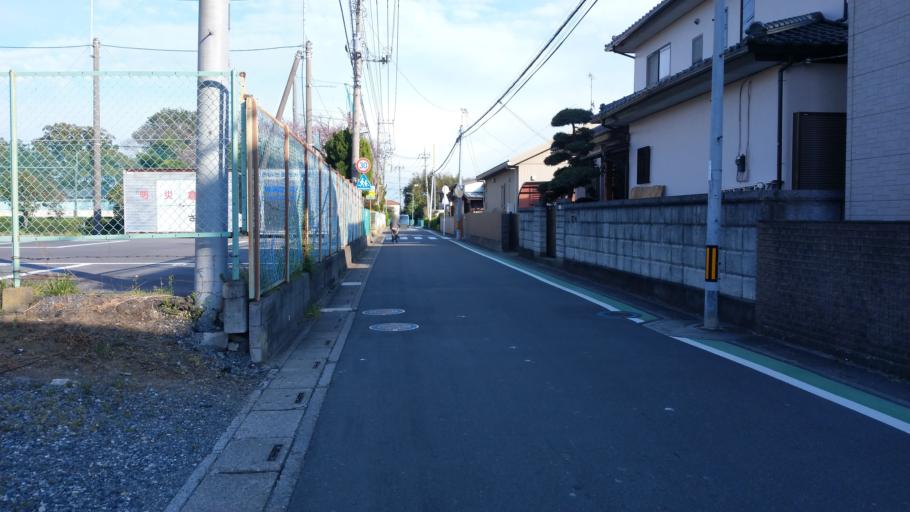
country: JP
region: Saitama
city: Yono
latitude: 35.8981
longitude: 139.5788
